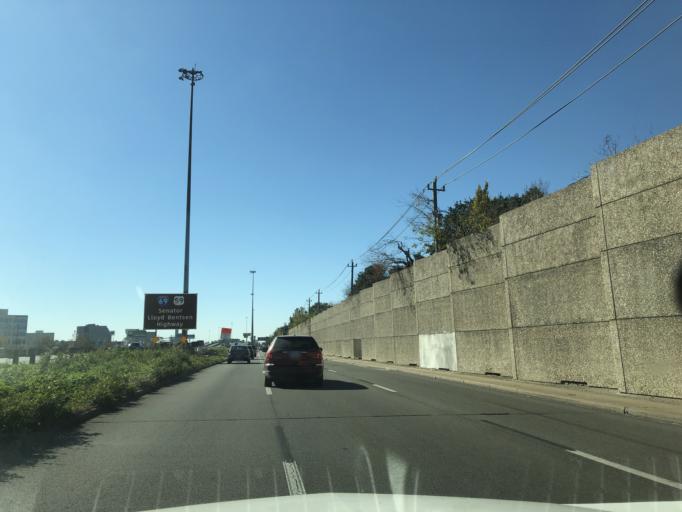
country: US
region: Texas
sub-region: Harris County
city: Piney Point Village
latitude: 29.6965
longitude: -95.5225
